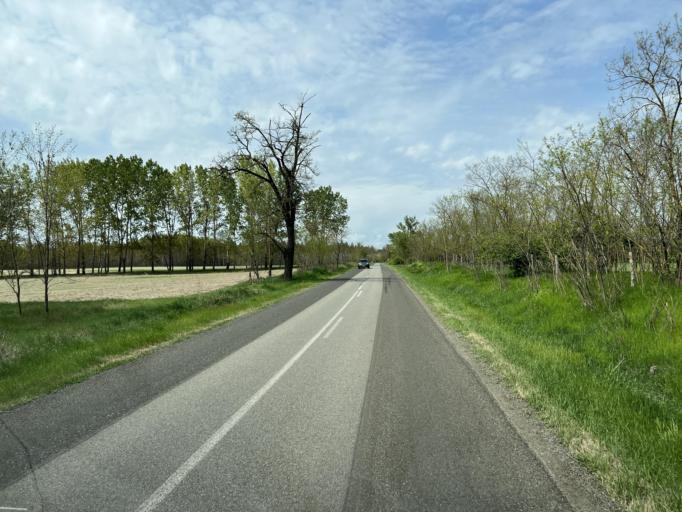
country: HU
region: Pest
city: Albertirsa
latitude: 47.1650
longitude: 19.6166
